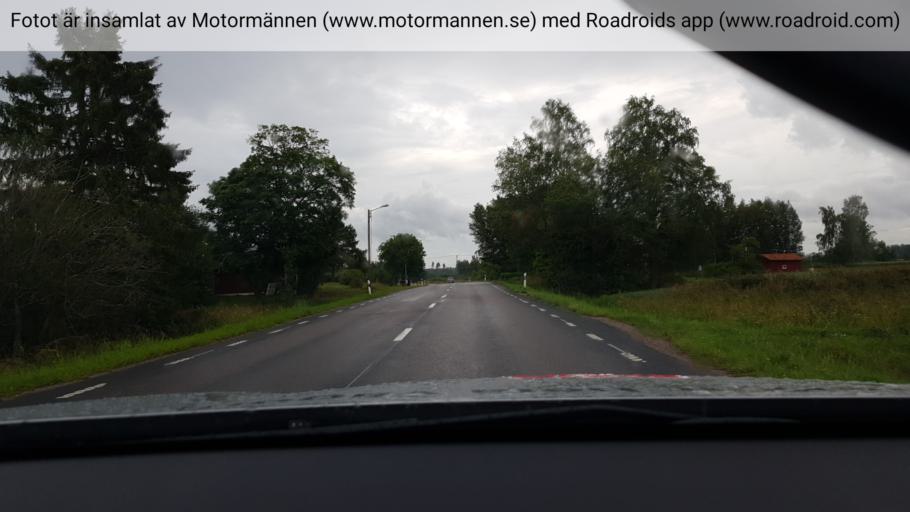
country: SE
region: Uppsala
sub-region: Tierps Kommun
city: Karlholmsbruk
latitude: 60.5073
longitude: 17.6582
